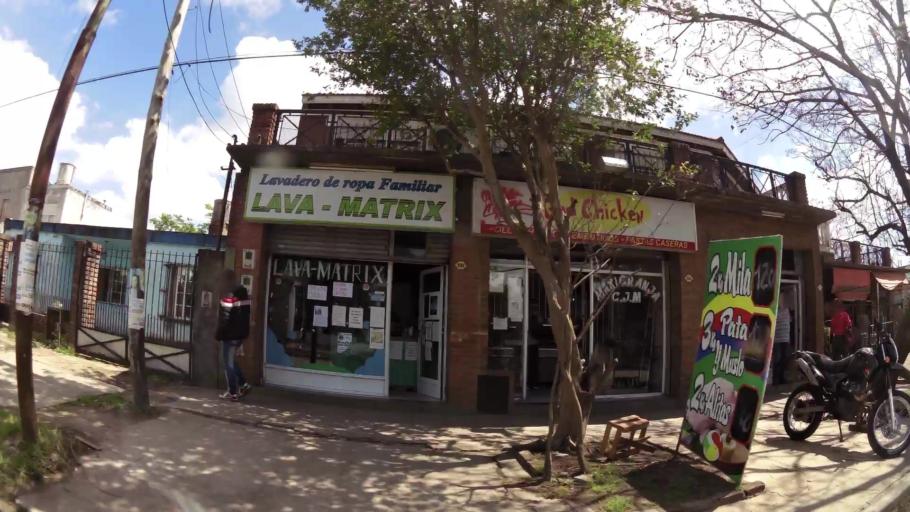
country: AR
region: Buenos Aires
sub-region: Partido de Quilmes
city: Quilmes
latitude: -34.8286
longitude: -58.2283
